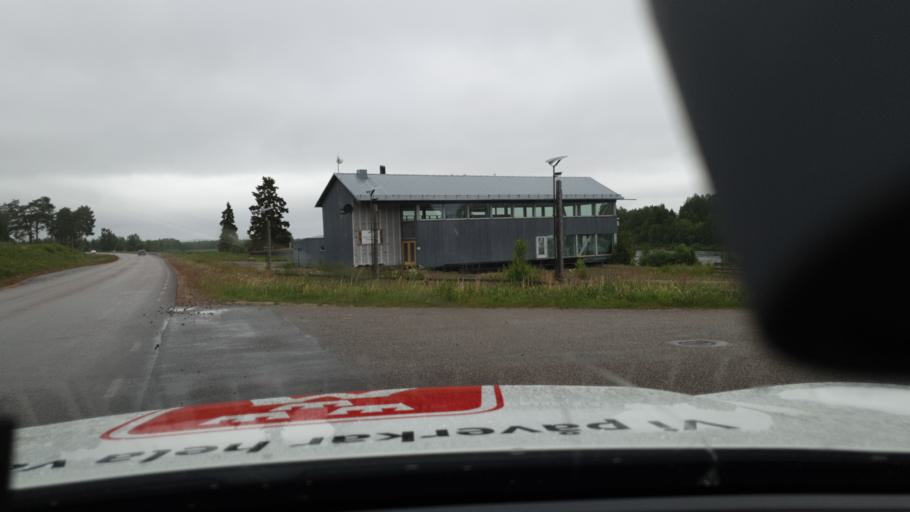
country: SE
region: Norrbotten
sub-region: Overtornea Kommun
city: OEvertornea
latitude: 66.5326
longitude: 23.7810
